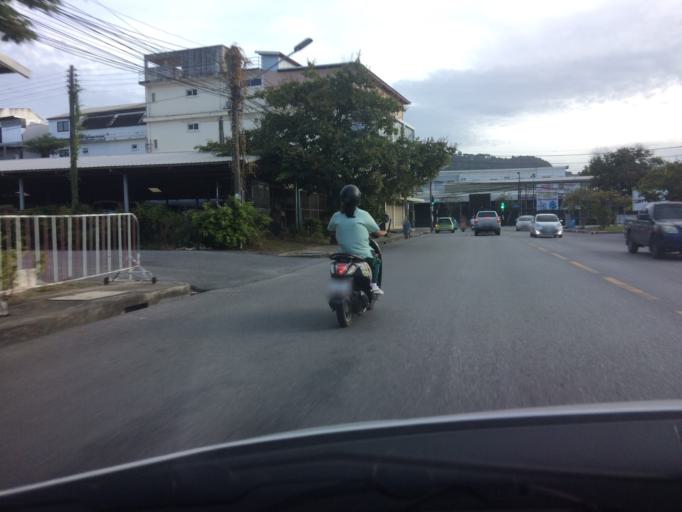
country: TH
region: Phuket
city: Ban Talat Yai
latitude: 7.8820
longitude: 98.3986
